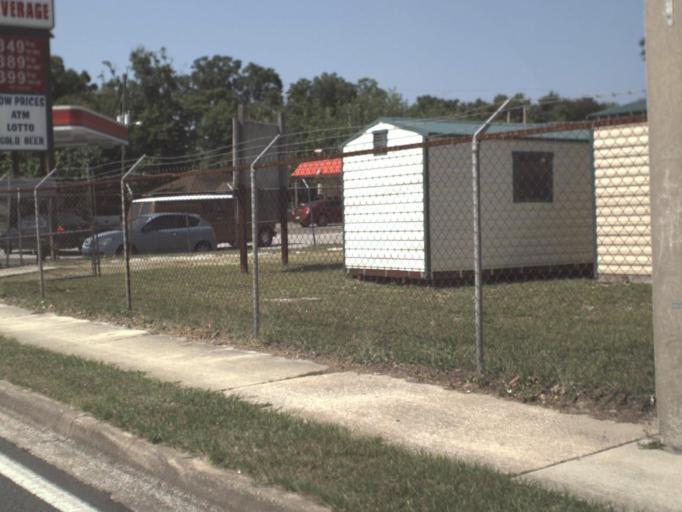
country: US
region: Florida
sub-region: Duval County
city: Jacksonville
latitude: 30.4002
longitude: -81.6839
